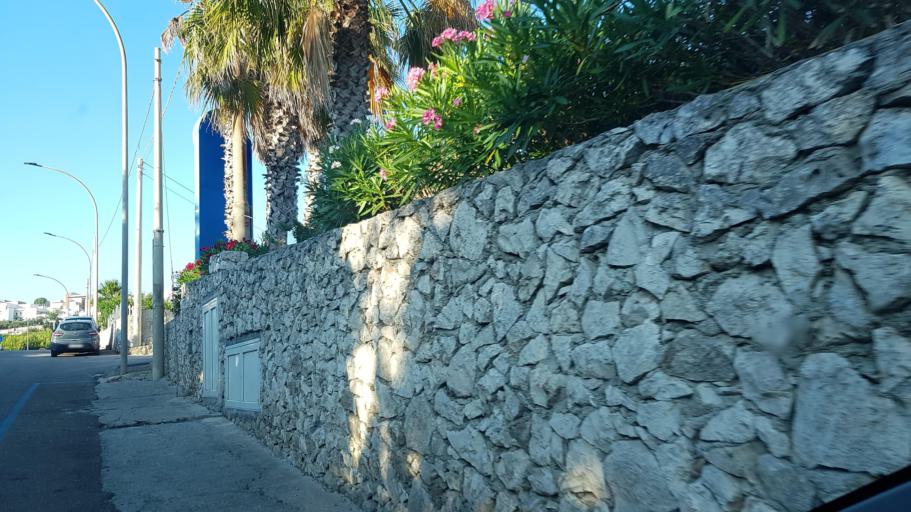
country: IT
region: Apulia
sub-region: Provincia di Lecce
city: Castro
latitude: 40.0024
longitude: 18.4229
